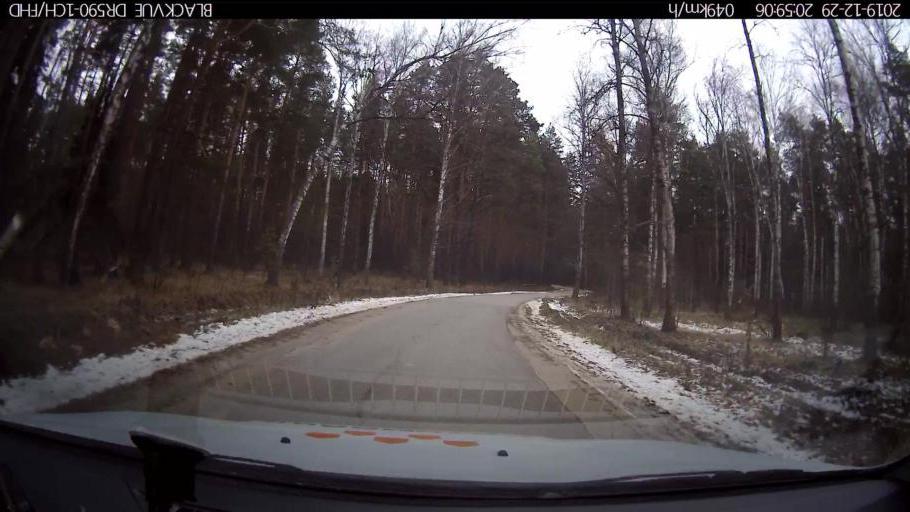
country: RU
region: Nizjnij Novgorod
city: Afonino
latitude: 56.1734
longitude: 43.9884
